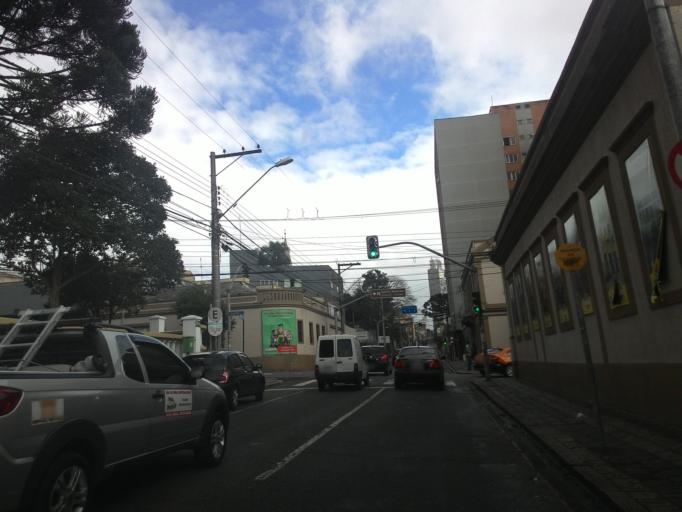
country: BR
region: Parana
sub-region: Curitiba
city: Curitiba
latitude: -25.4255
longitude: -49.2730
